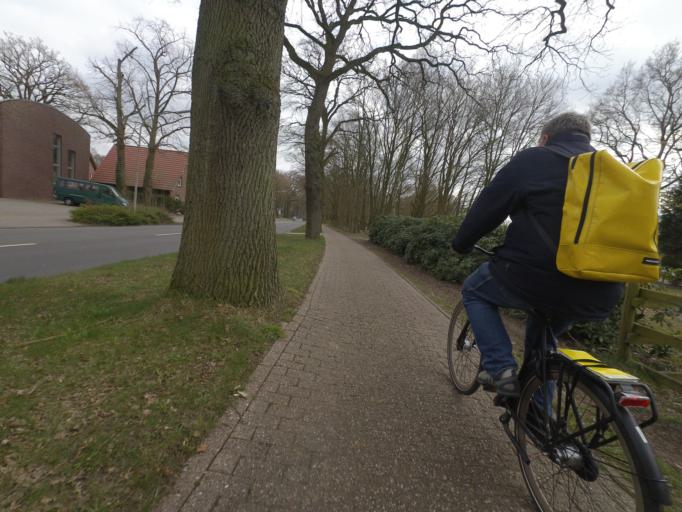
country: DE
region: Lower Saxony
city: Wardenburg
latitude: 53.0963
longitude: 8.2077
